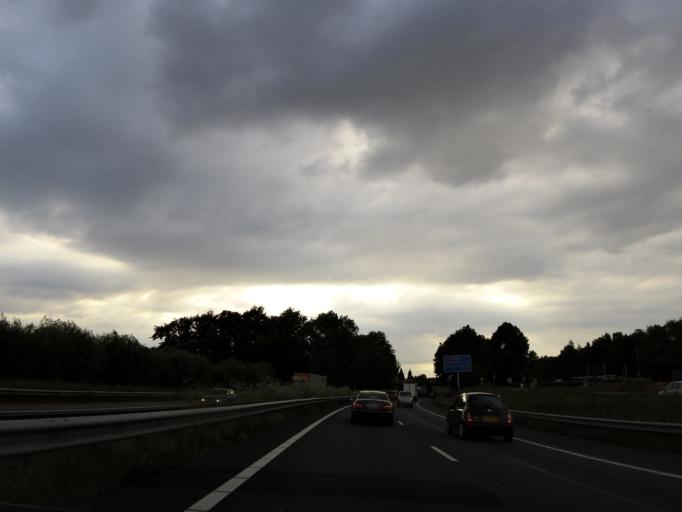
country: NL
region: Limburg
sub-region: Gemeente Schinnen
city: Puth
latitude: 50.9425
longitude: 5.8507
